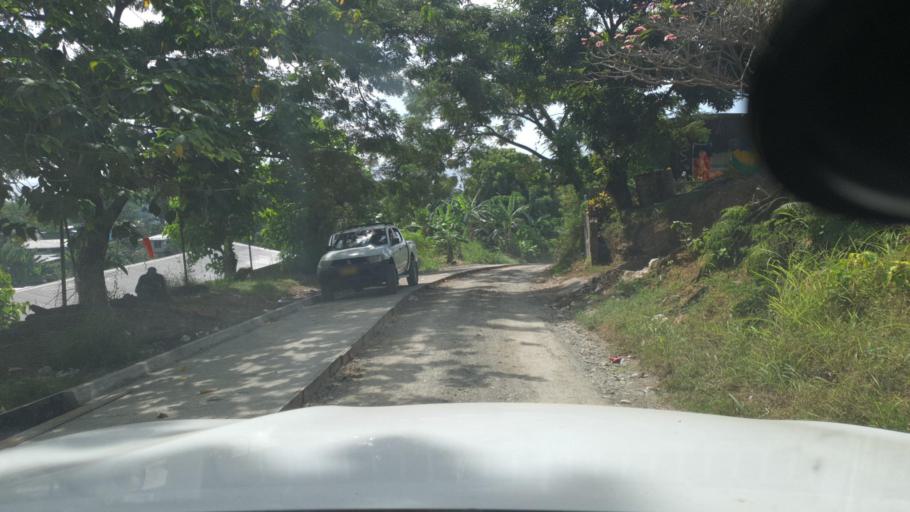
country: SB
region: Guadalcanal
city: Honiara
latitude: -9.4382
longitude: 159.9865
